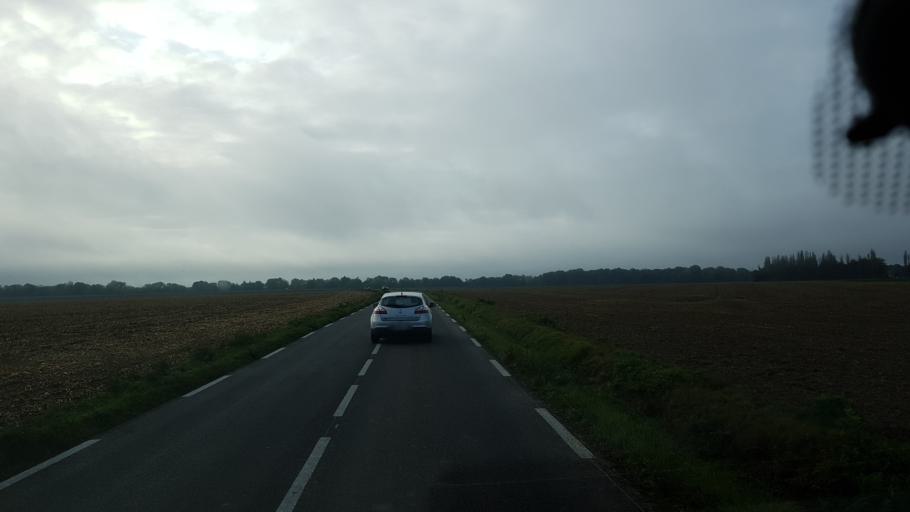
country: FR
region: Ile-de-France
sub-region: Departement de l'Essonne
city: Les Molieres
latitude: 48.6594
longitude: 2.0664
